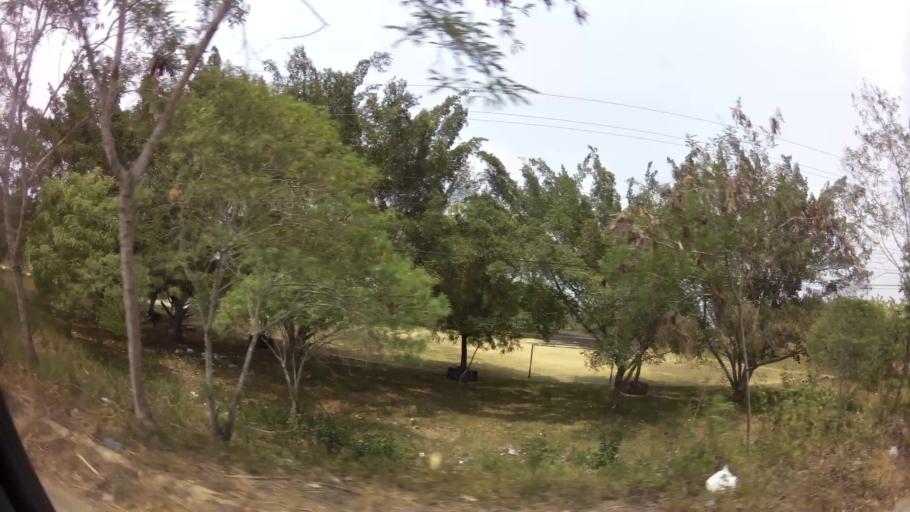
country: HN
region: Cortes
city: La Lima
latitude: 15.4267
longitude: -87.8994
